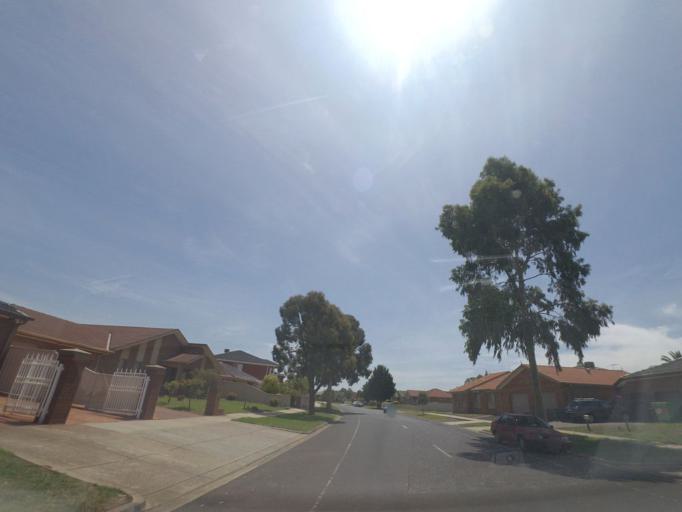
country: AU
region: Victoria
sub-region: Brimbank
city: Keilor Downs
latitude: -37.7165
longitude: 144.8003
